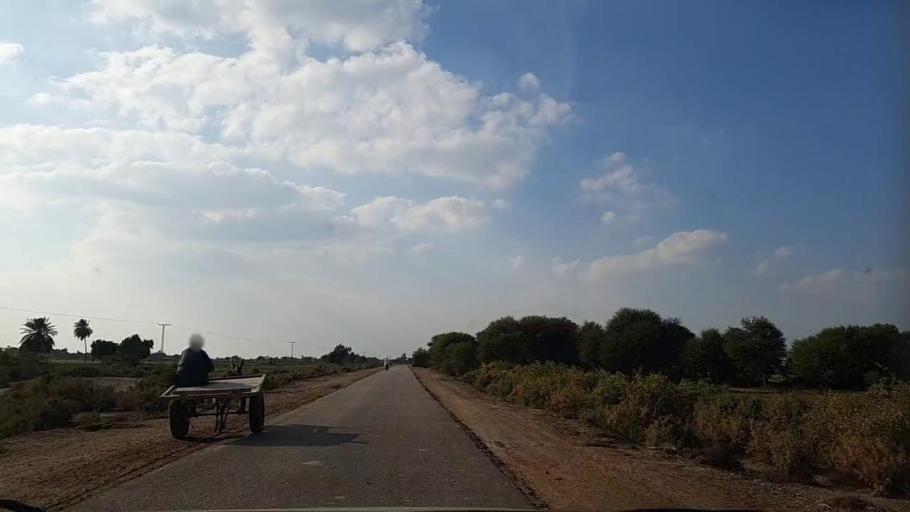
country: PK
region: Sindh
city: Pithoro
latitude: 25.6688
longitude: 69.2333
